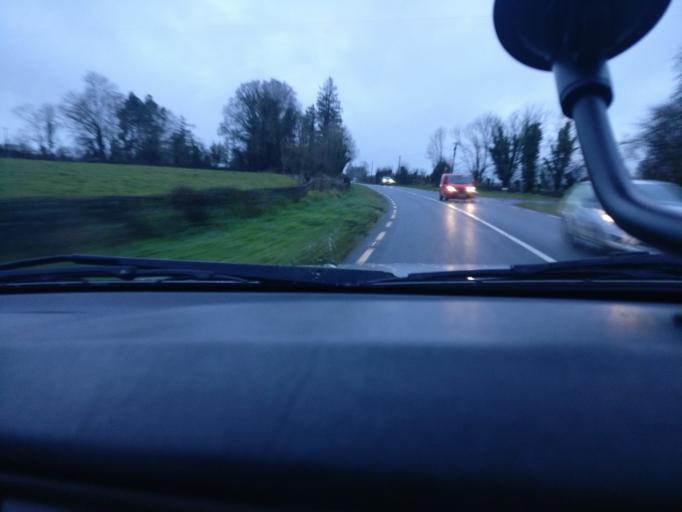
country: IE
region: Connaught
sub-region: County Galway
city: Ballinasloe
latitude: 53.2824
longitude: -8.3672
